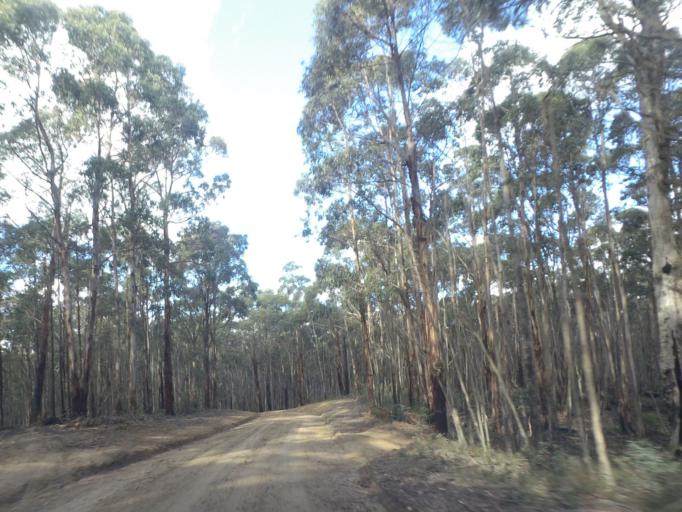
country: AU
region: Victoria
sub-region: Moorabool
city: Bacchus Marsh
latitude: -37.4521
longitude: 144.4597
